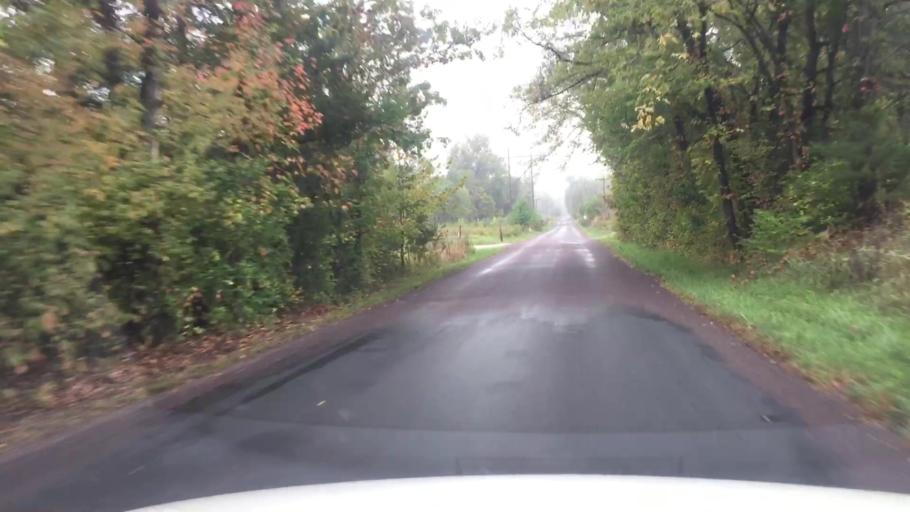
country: US
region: Missouri
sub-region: Boone County
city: Columbia
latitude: 38.8697
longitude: -92.3738
